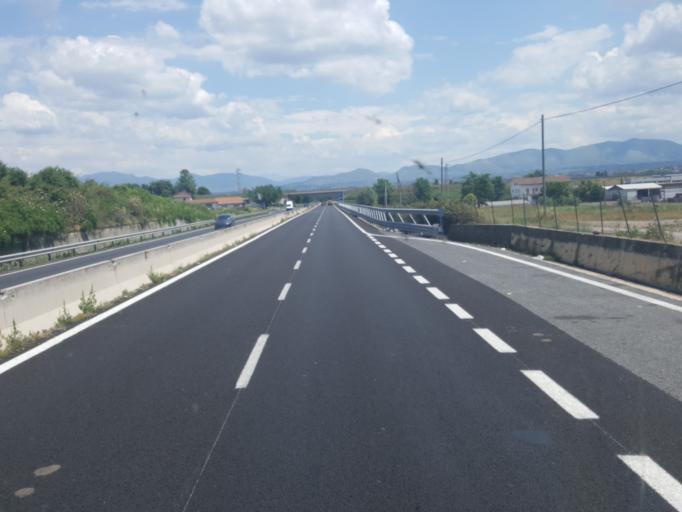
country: IT
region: Latium
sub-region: Citta metropolitana di Roma Capitale
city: Fiano Romano
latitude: 42.1447
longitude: 12.6160
